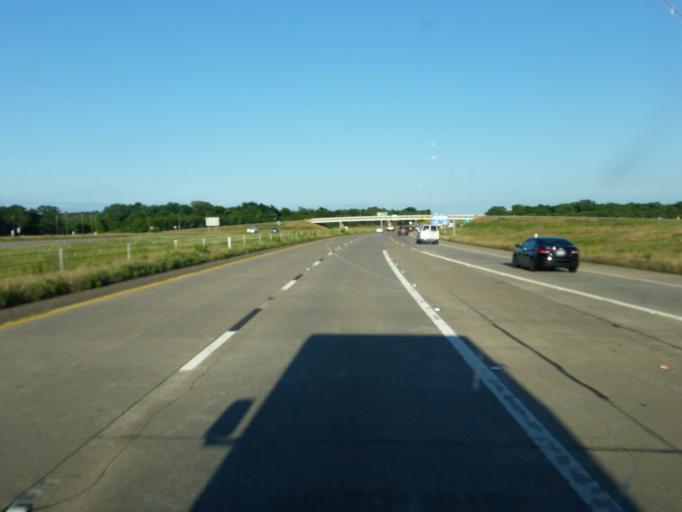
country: US
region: Texas
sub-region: Kaufman County
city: Terrell
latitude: 32.7136
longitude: -96.3044
